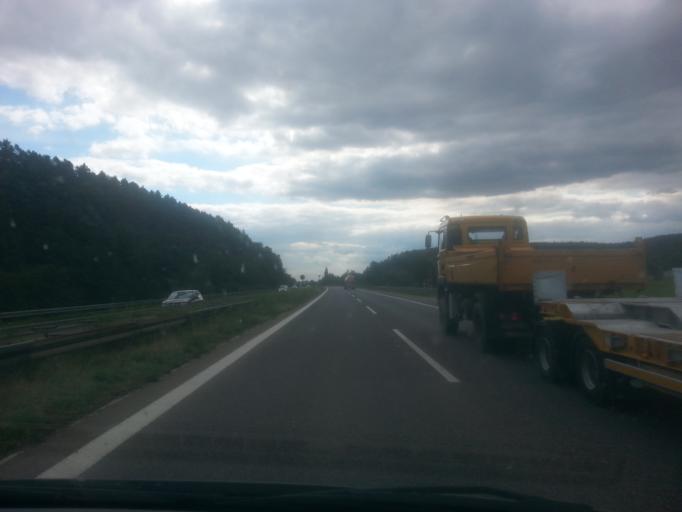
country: DE
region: Bavaria
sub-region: Upper Palatinate
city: Nabburg
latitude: 49.4281
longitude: 12.1736
